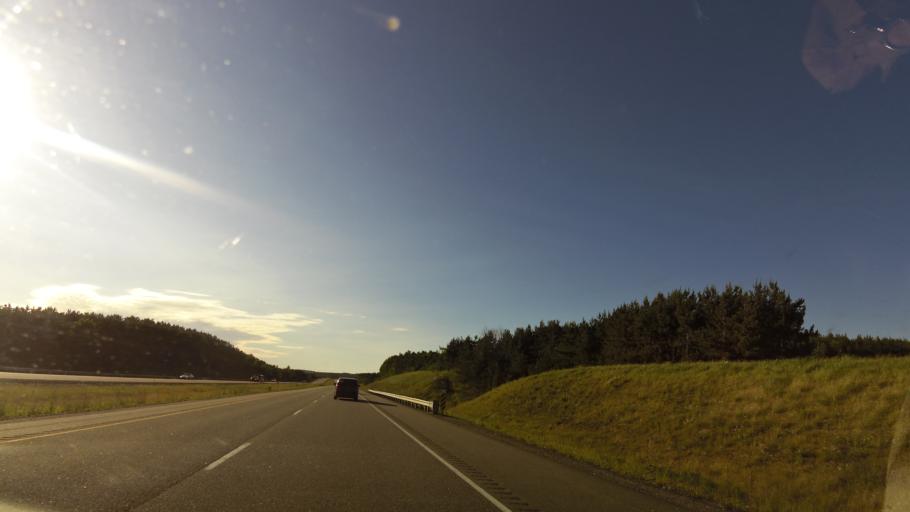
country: CA
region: Ontario
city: Barrie
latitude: 44.5118
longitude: -79.7288
